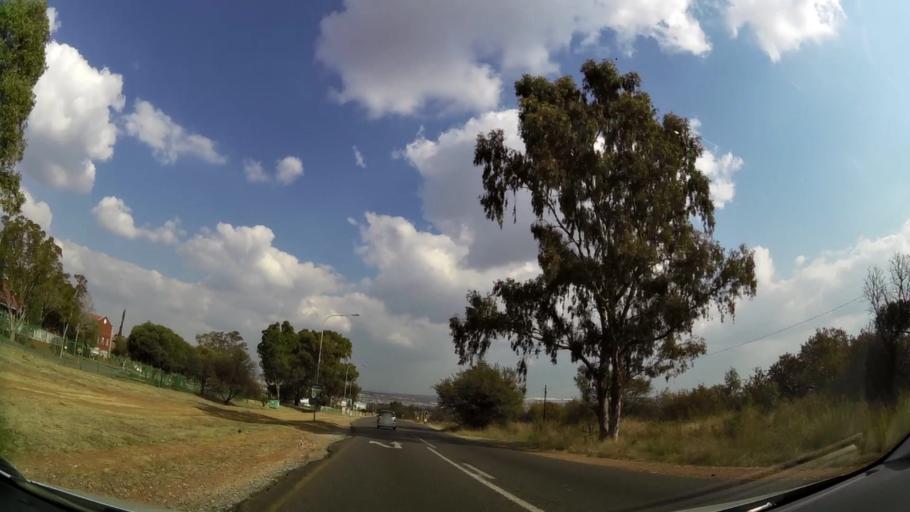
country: ZA
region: Gauteng
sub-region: City of Tshwane Metropolitan Municipality
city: Centurion
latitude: -25.8715
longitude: 28.2335
